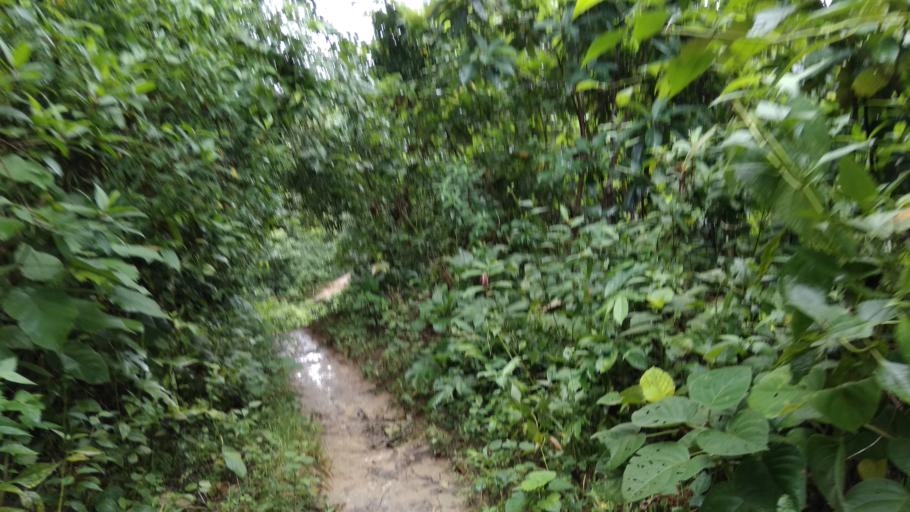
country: IN
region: Tripura
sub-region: Dhalai
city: Kamalpur
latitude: 24.1722
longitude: 91.8887
